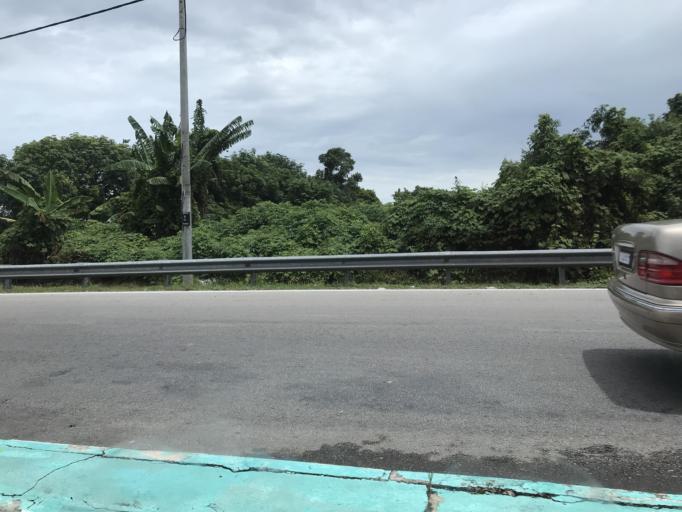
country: MY
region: Kelantan
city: Tumpat
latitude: 6.1669
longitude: 102.1910
